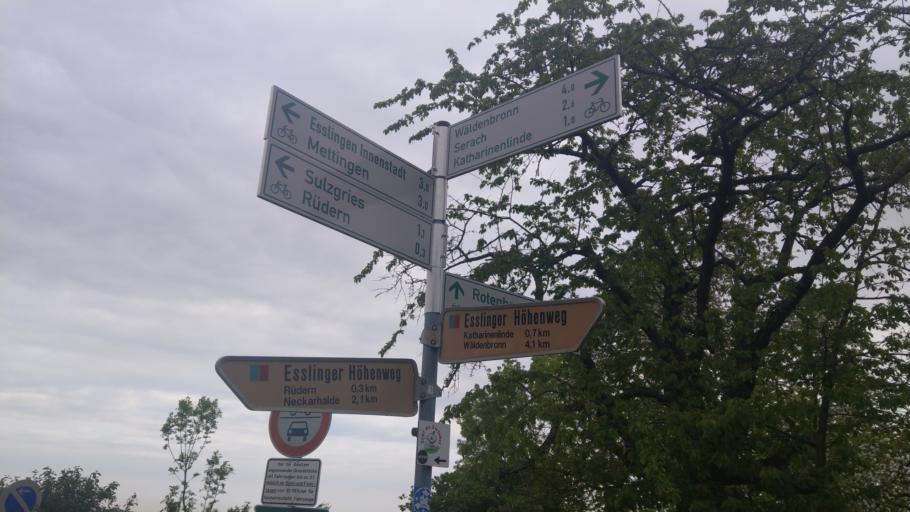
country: DE
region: Baden-Wuerttemberg
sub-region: Regierungsbezirk Stuttgart
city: Esslingen
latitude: 48.7678
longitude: 9.2854
